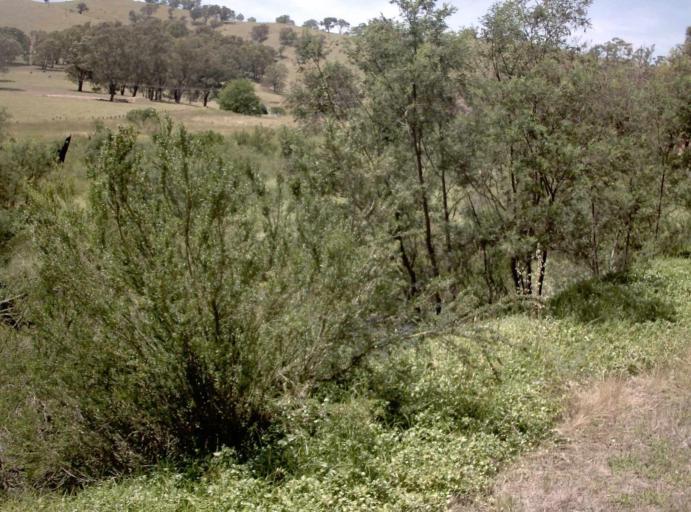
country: AU
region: Victoria
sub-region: East Gippsland
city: Bairnsdale
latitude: -37.3903
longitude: 147.8295
